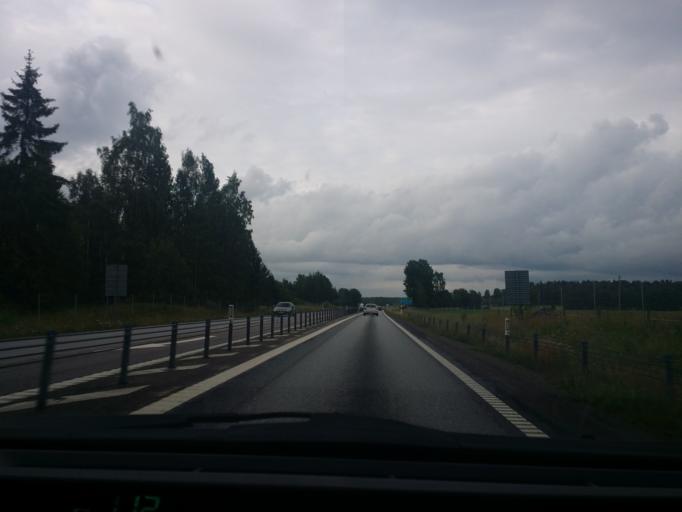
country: SE
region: Vaestmanland
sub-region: Kopings Kommun
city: Koping
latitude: 59.5630
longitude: 16.0677
